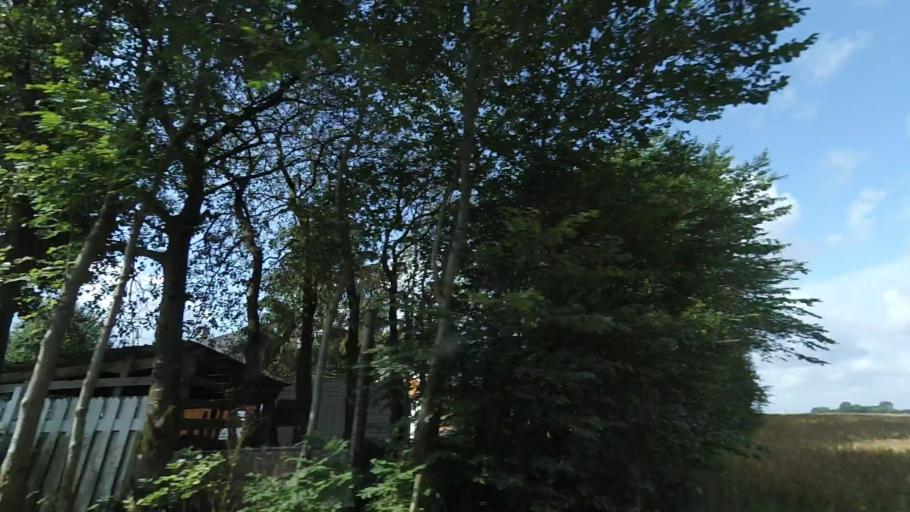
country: DK
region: Central Jutland
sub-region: Syddjurs Kommune
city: Ryomgard
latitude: 56.4704
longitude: 10.5114
